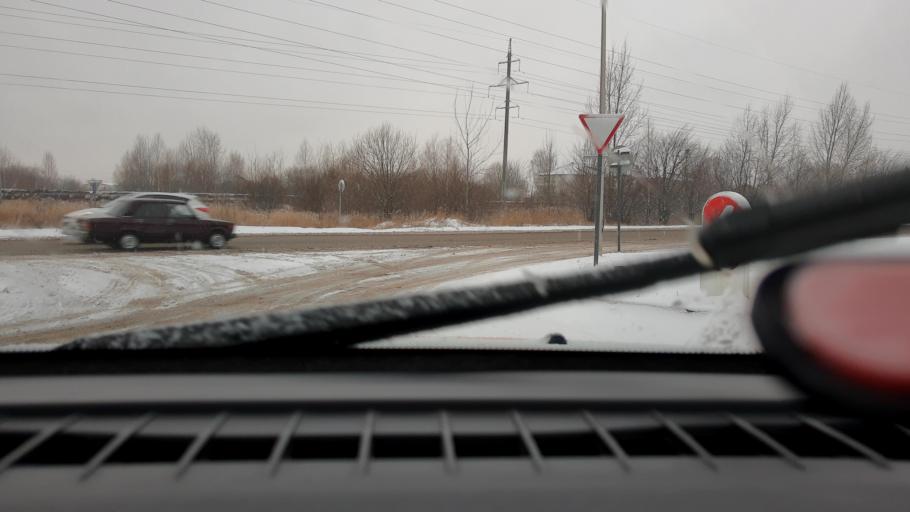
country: RU
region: Nizjnij Novgorod
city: Novaya Balakhna
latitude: 56.4776
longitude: 43.6068
